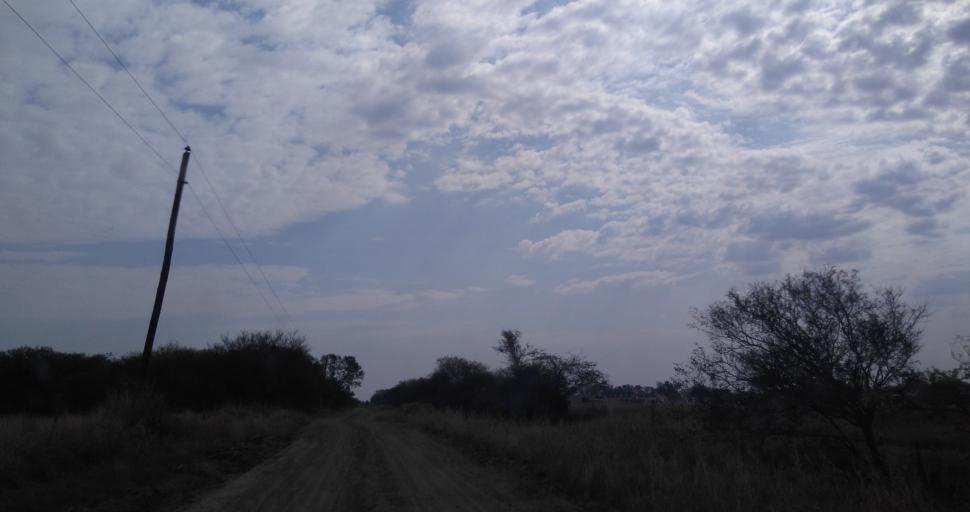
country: AR
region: Chaco
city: Fontana
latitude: -27.4614
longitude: -59.0467
